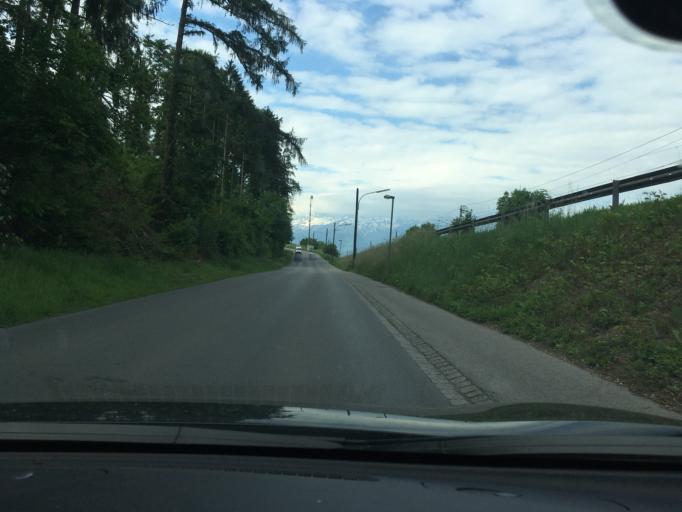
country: AT
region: Vorarlberg
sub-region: Politischer Bezirk Feldkirch
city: Nofels
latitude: 47.2347
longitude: 9.5798
